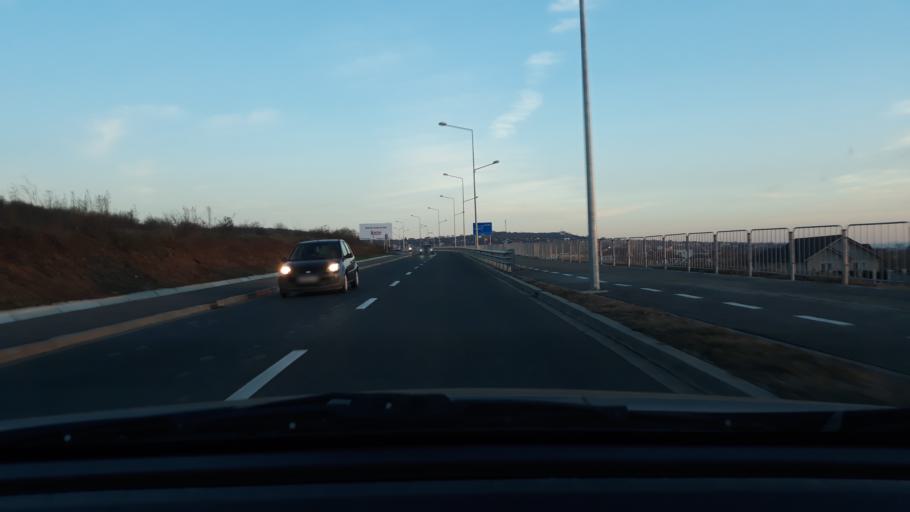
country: RO
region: Bihor
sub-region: Comuna Biharea
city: Oradea
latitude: 47.0982
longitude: 21.9194
